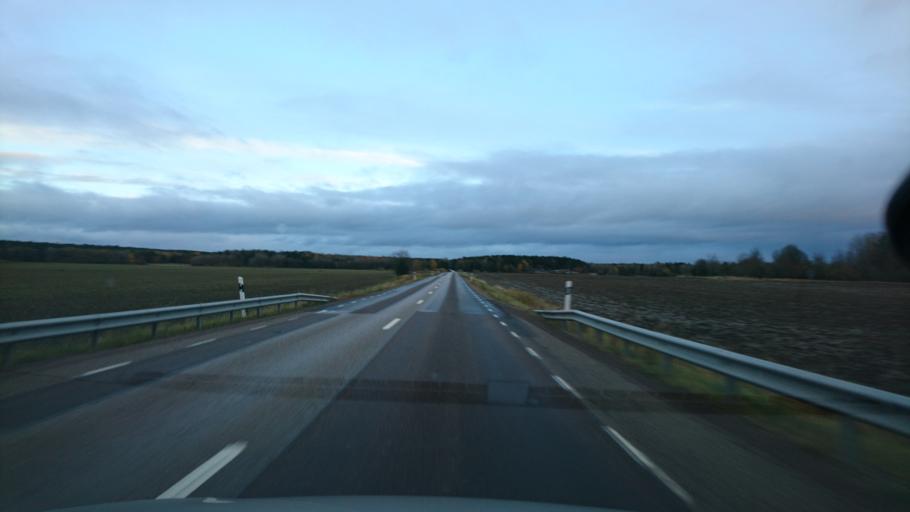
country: SE
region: Uppsala
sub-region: Uppsala Kommun
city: Vattholma
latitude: 59.9502
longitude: 17.9154
